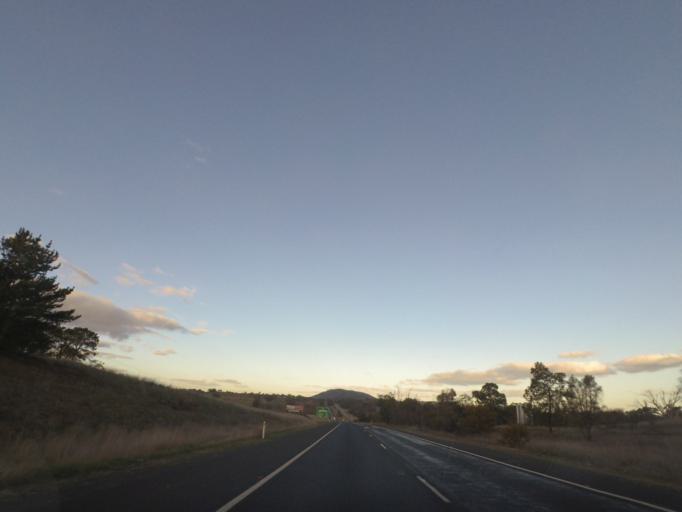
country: AU
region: New South Wales
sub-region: Yass Valley
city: Yass
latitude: -34.7678
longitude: 148.7715
